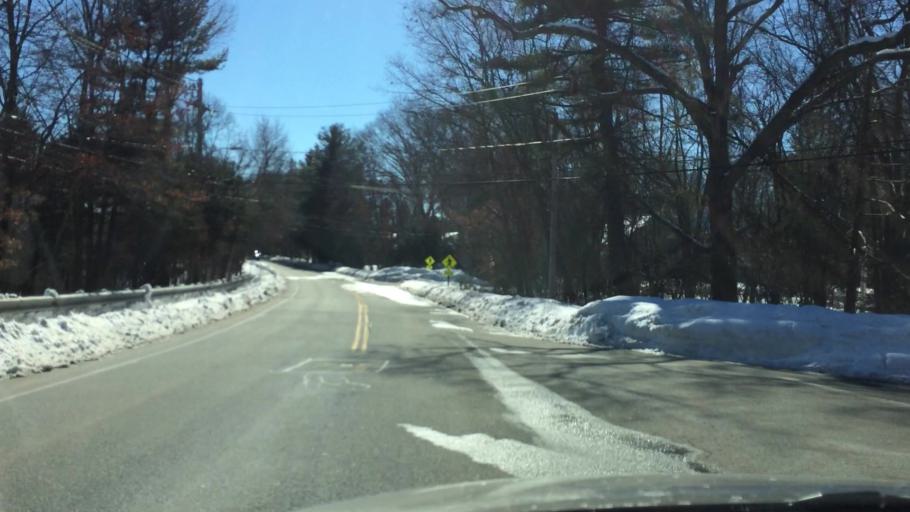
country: US
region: Massachusetts
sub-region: Middlesex County
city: Bedford
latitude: 42.5170
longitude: -71.2593
